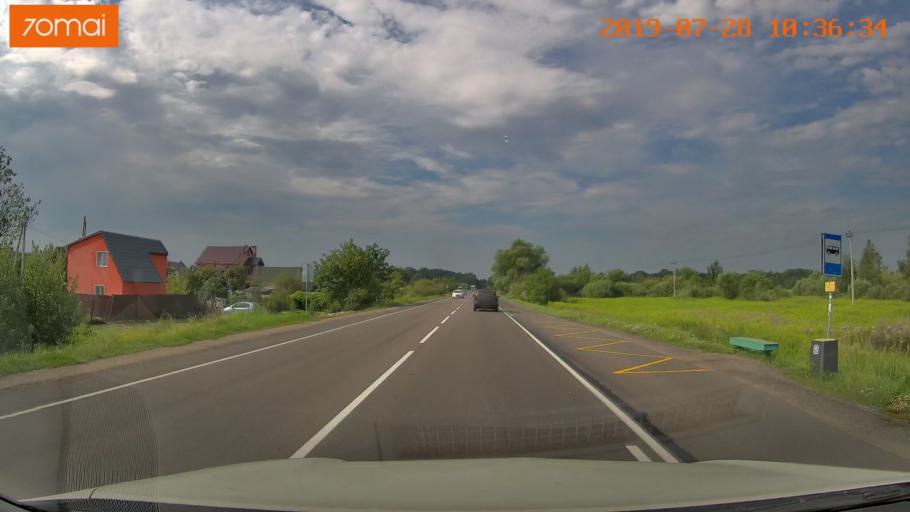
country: RU
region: Kaliningrad
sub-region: Gorod Kaliningrad
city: Kaliningrad
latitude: 54.7373
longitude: 20.4200
